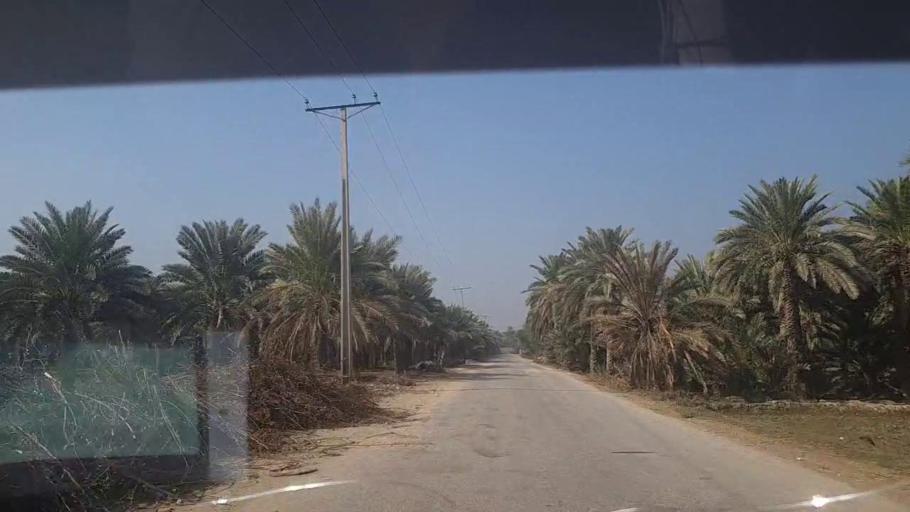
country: PK
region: Sindh
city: Kot Diji
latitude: 27.3764
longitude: 68.6941
